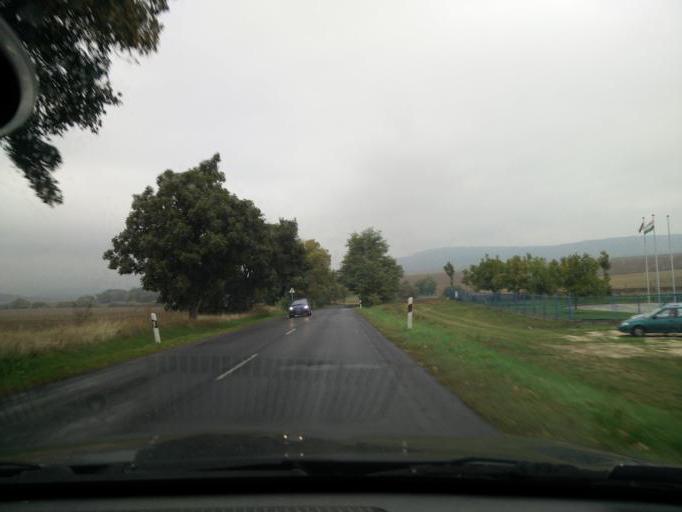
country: HU
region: Komarom-Esztergom
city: Tarjan
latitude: 47.6166
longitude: 18.5130
